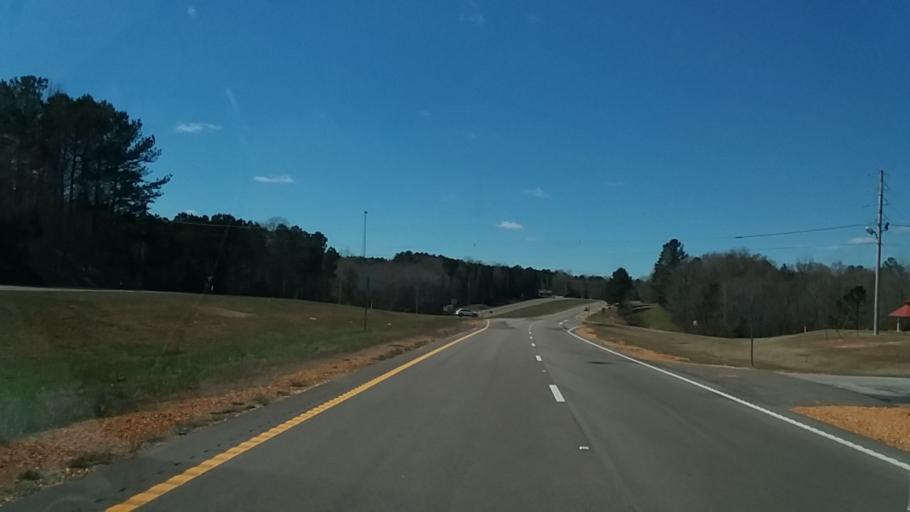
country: US
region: Mississippi
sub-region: Alcorn County
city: Farmington
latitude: 34.8625
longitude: -88.4107
